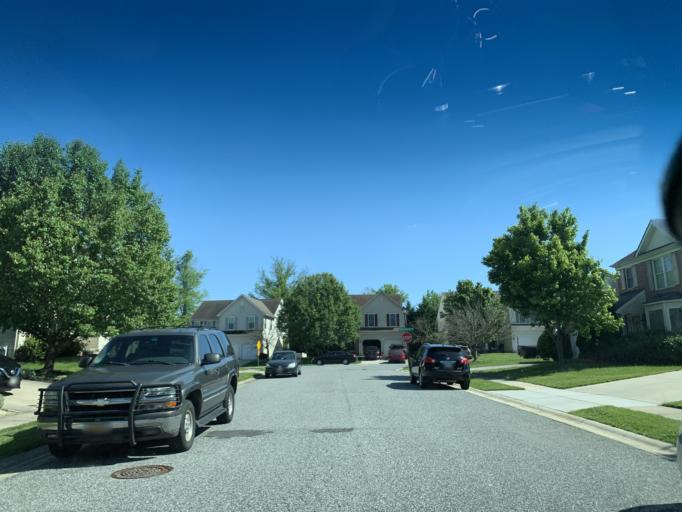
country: US
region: Maryland
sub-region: Harford County
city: Riverside
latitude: 39.4902
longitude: -76.2222
